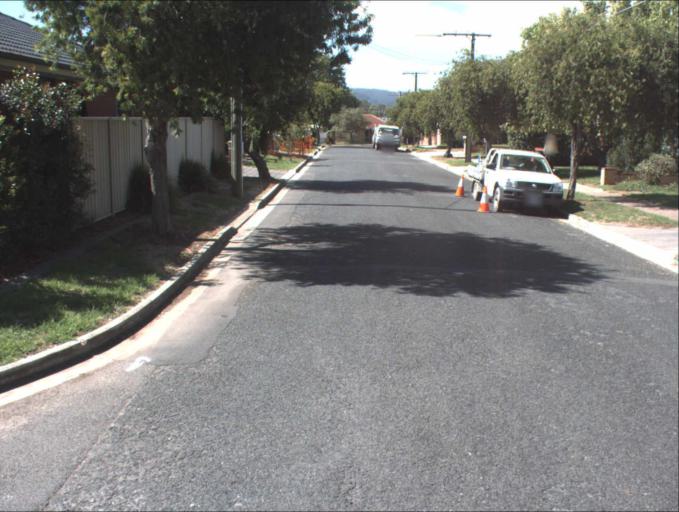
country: AU
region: South Australia
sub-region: Port Adelaide Enfield
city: Klemzig
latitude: -34.8783
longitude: 138.6400
